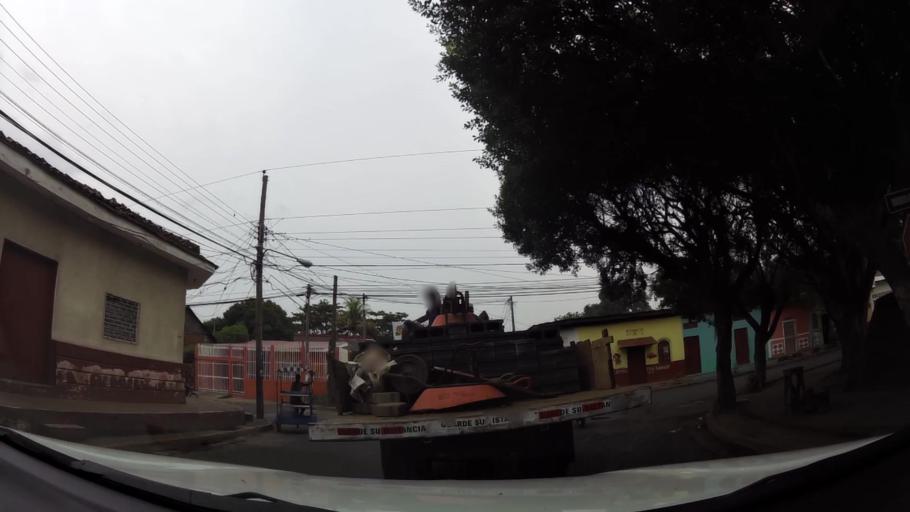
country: NI
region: Leon
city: Leon
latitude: 12.4467
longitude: -86.8742
